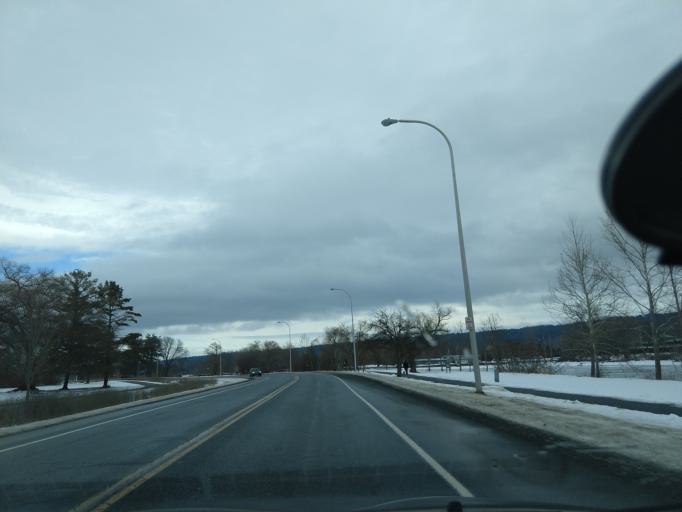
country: US
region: New York
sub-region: Tompkins County
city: Ithaca
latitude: 42.4495
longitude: -76.5125
